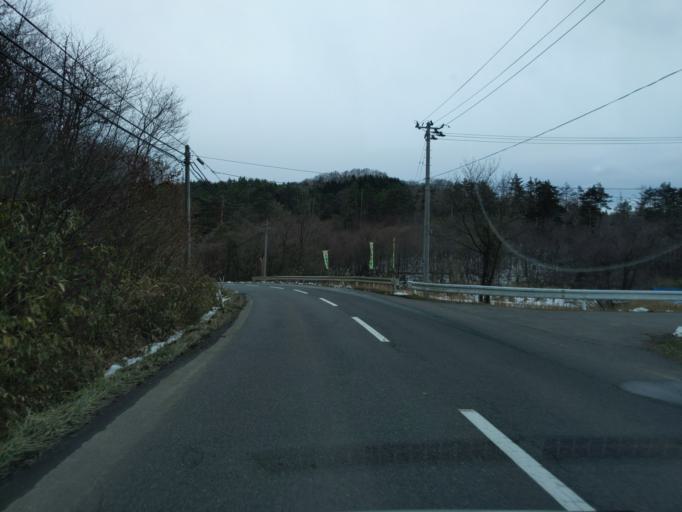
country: JP
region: Iwate
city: Mizusawa
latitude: 39.1289
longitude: 141.2490
